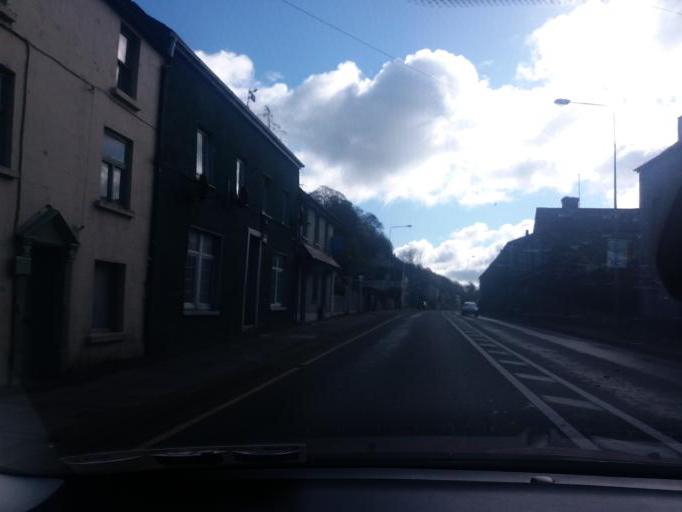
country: IE
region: Munster
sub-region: County Cork
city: Cork
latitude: 51.9028
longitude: -8.4493
